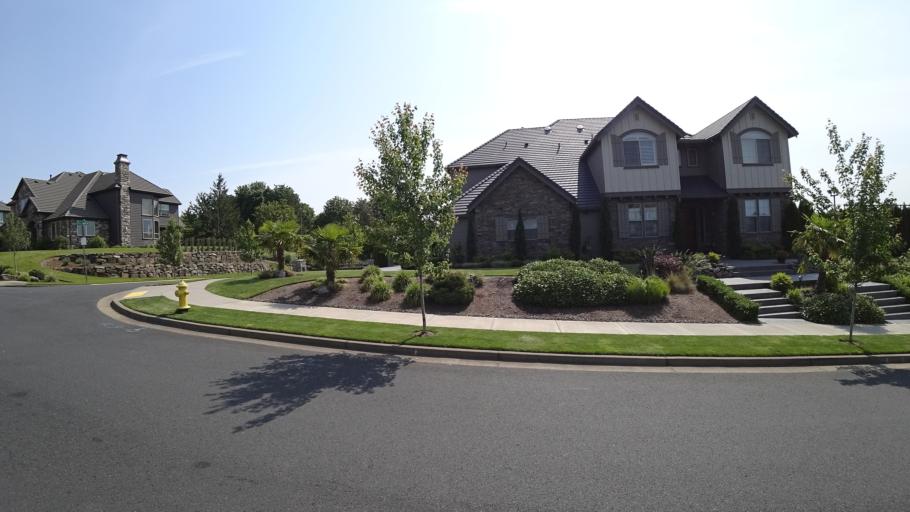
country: US
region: Oregon
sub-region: Clackamas County
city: Happy Valley
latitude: 45.4597
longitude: -122.5129
